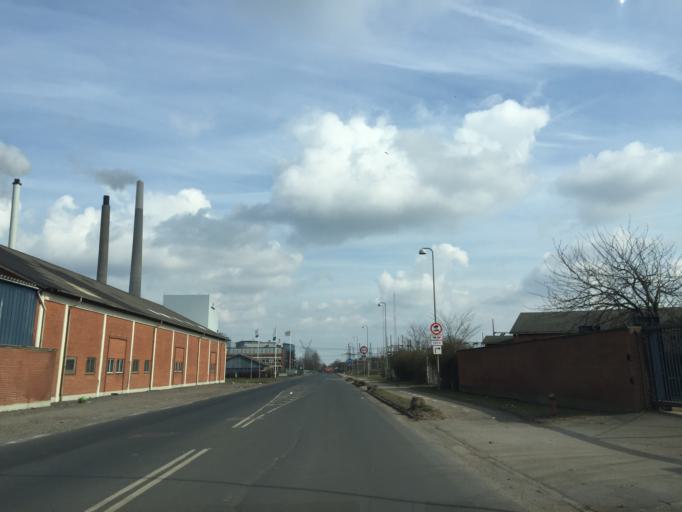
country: DK
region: South Denmark
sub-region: Odense Kommune
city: Stige
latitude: 55.4265
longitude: 10.4008
